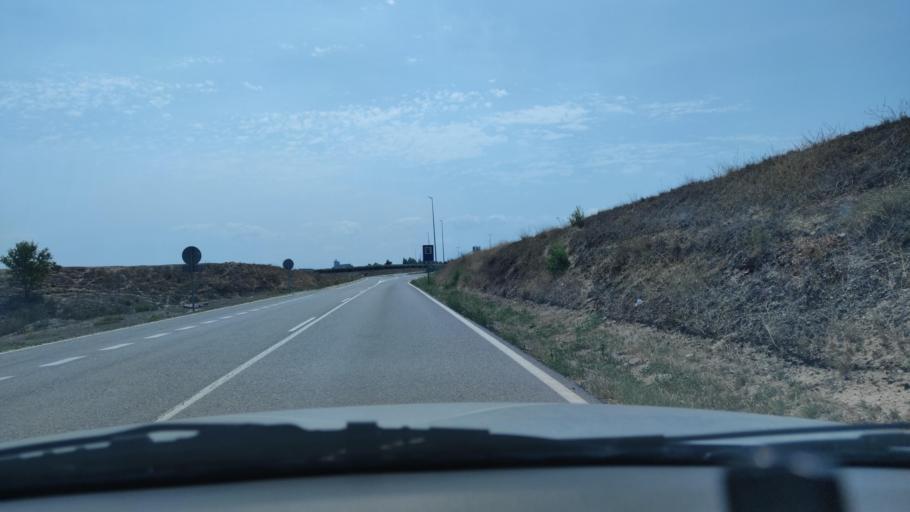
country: ES
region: Catalonia
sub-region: Provincia de Lleida
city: Bellpuig
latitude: 41.6454
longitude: 0.9996
